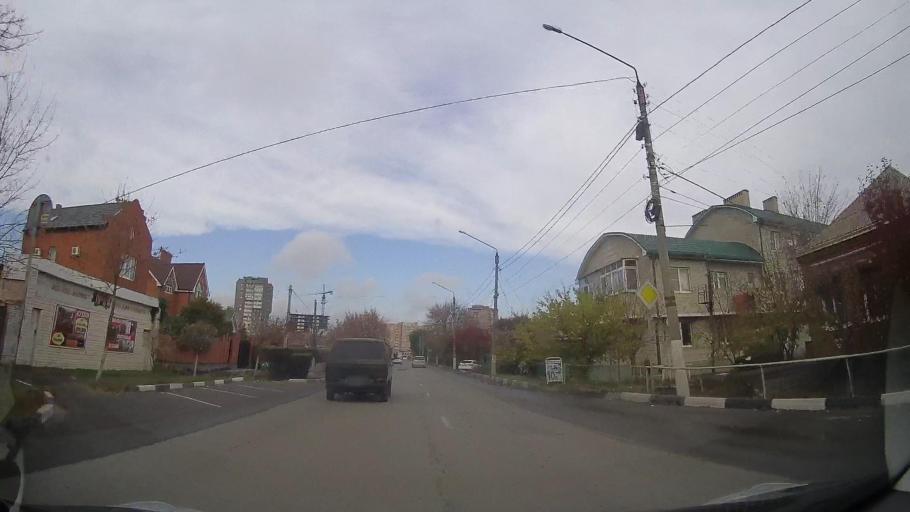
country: RU
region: Rostov
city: Bataysk
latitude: 47.1528
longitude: 39.7471
